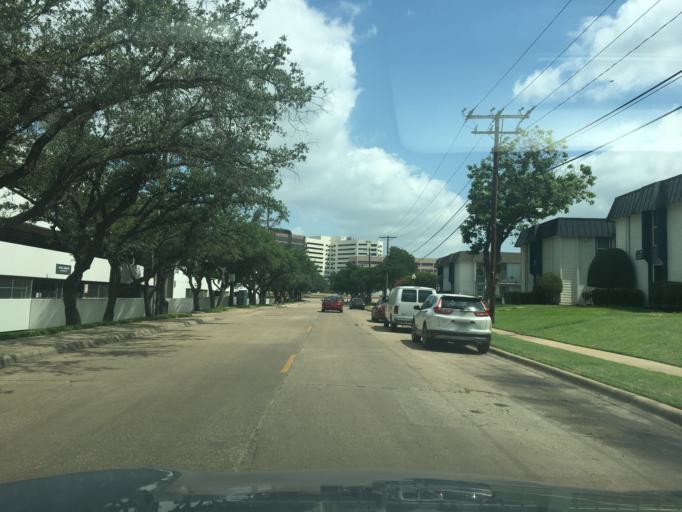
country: US
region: Texas
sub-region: Dallas County
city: Addison
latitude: 32.9226
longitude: -96.8151
